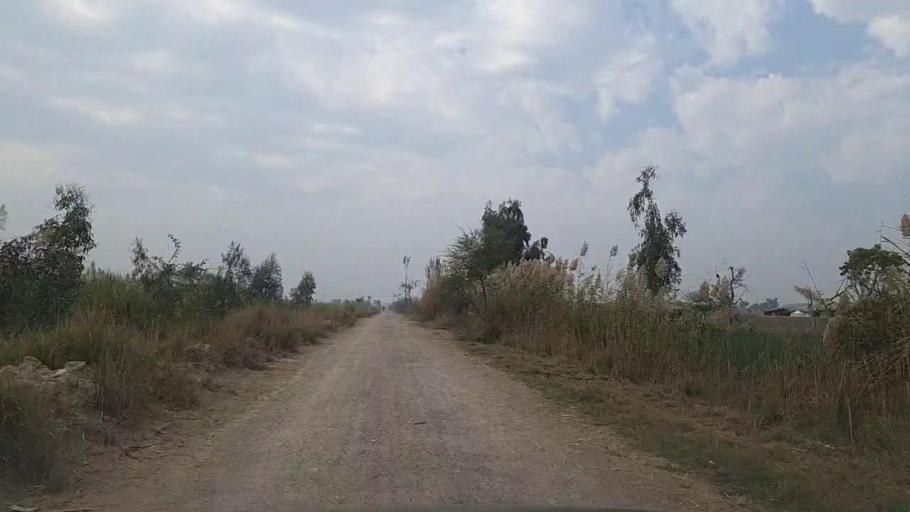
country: PK
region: Sindh
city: Nawabshah
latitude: 26.3609
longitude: 68.3840
